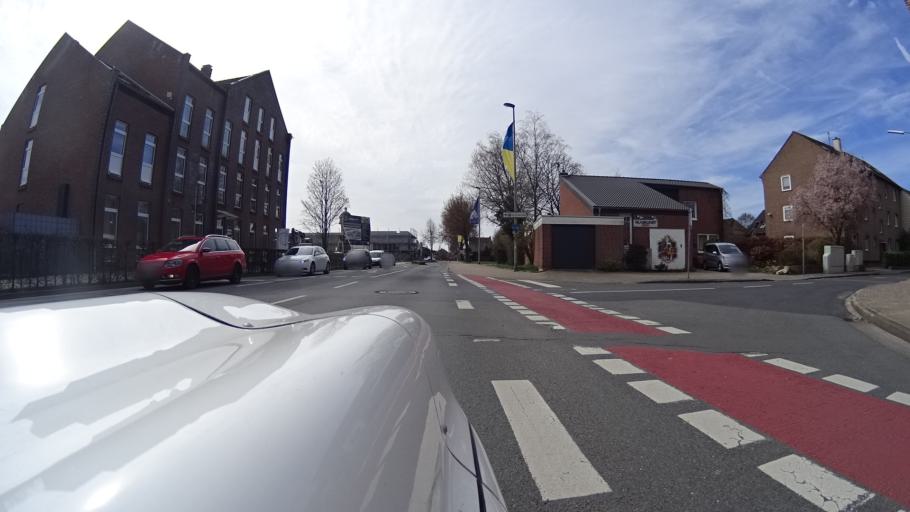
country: DE
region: North Rhine-Westphalia
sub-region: Regierungsbezirk Dusseldorf
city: Kevelaer
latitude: 51.5854
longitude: 6.2409
